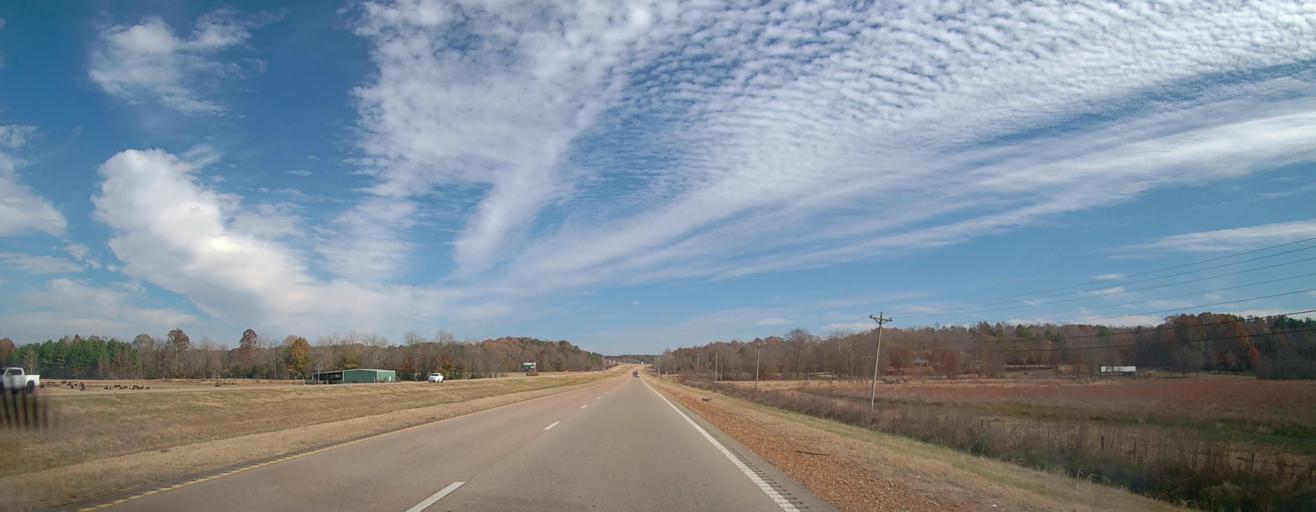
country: US
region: Mississippi
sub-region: Tippah County
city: Ripley
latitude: 34.9537
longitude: -88.8706
